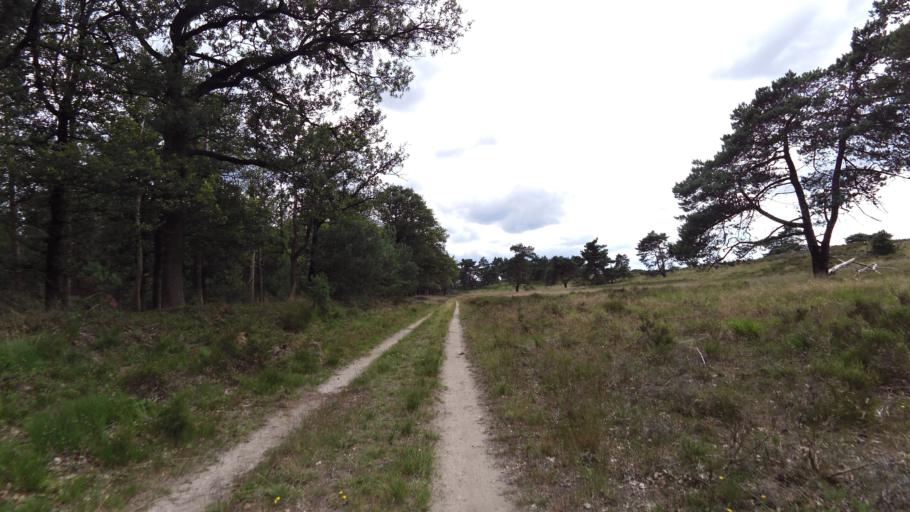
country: NL
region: Gelderland
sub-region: Gemeente Apeldoorn
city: Uddel
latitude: 52.2048
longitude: 5.8619
